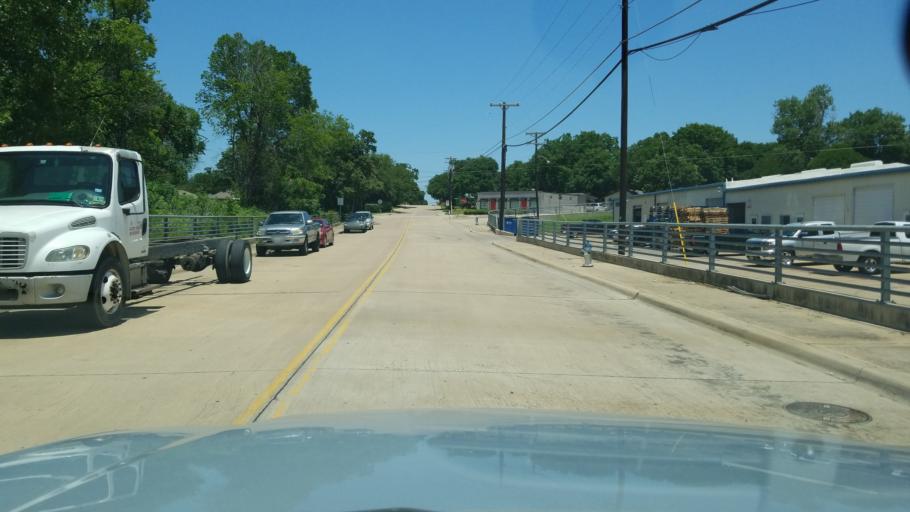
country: US
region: Texas
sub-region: Dallas County
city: Irving
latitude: 32.8027
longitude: -96.9170
